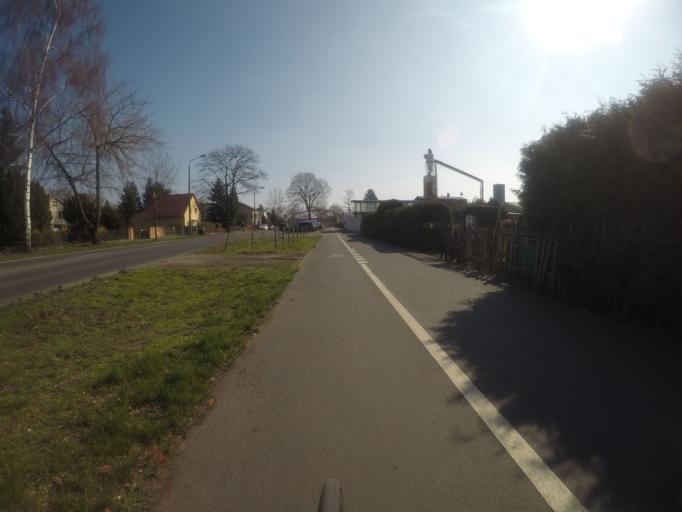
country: DE
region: Berlin
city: Adlershof
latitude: 52.4475
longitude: 13.5546
